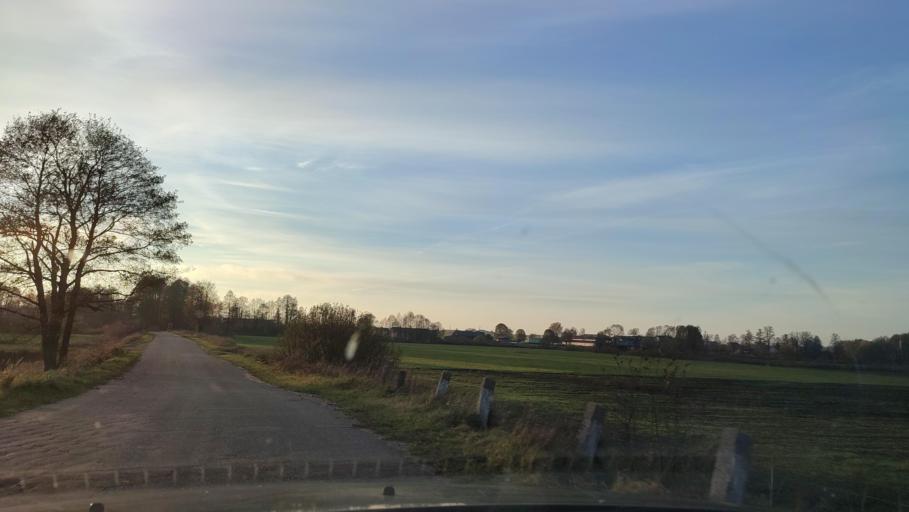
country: PL
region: Masovian Voivodeship
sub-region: Powiat mlawski
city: Dzierzgowo
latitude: 53.2602
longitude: 20.6115
